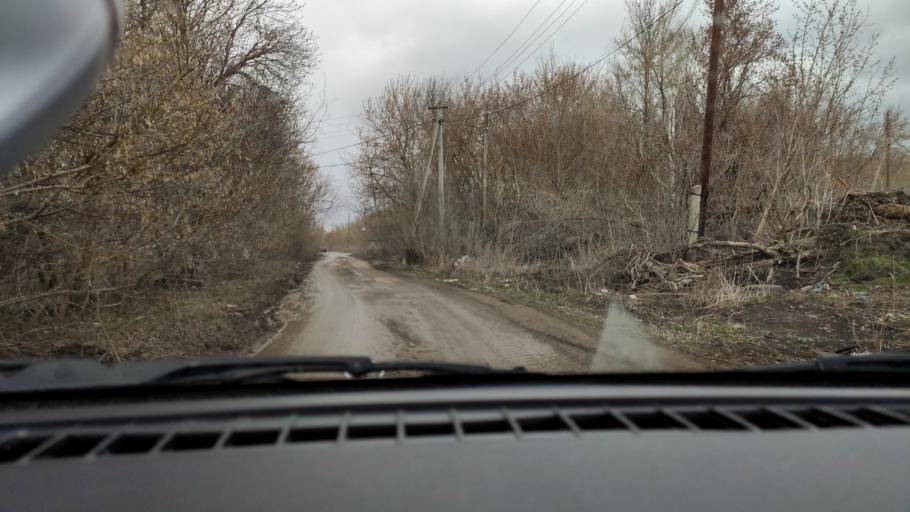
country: RU
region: Samara
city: Petra-Dubrava
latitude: 53.3222
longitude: 50.2936
